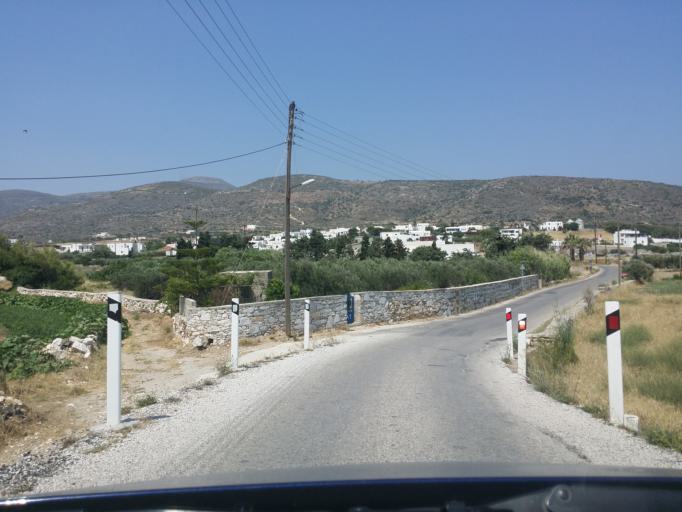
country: GR
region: South Aegean
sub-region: Nomos Kykladon
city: Naousa
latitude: 37.0516
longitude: 25.2444
